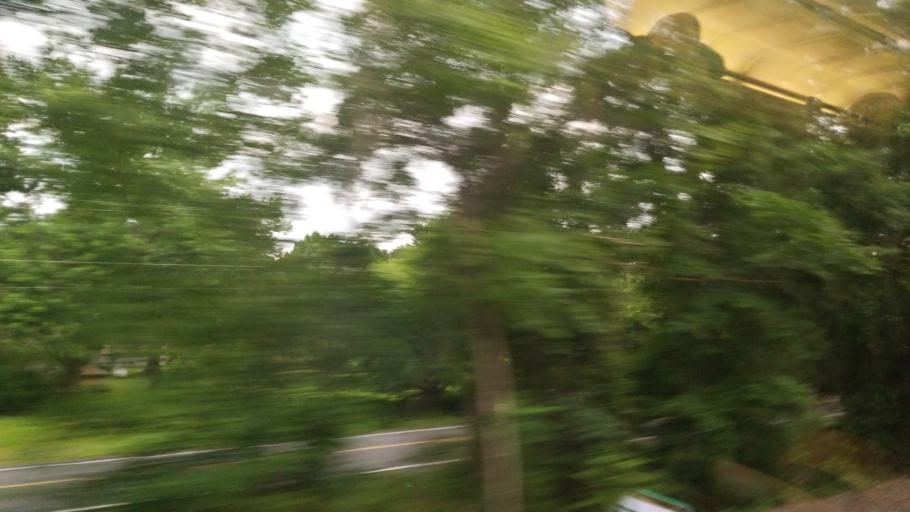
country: US
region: Virginia
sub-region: Culpeper County
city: Culpeper
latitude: 38.4171
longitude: -78.0055
